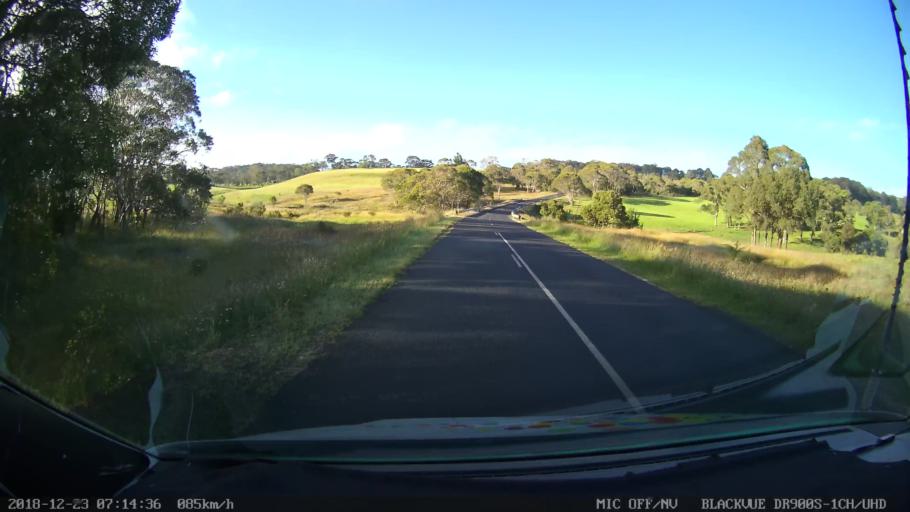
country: AU
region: New South Wales
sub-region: Bellingen
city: Dorrigo
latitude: -30.4371
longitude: 152.3214
